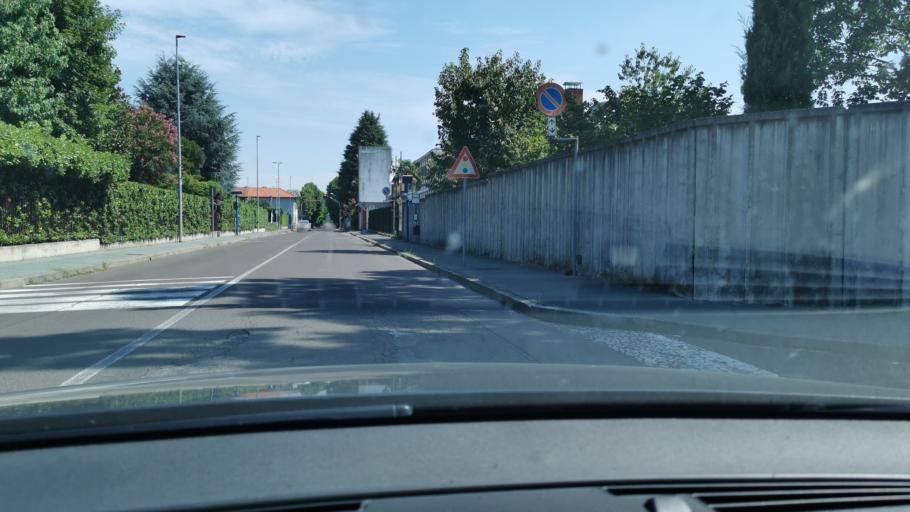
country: IT
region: Lombardy
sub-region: Citta metropolitana di Milano
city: Rescaldina
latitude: 45.6199
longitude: 8.9538
